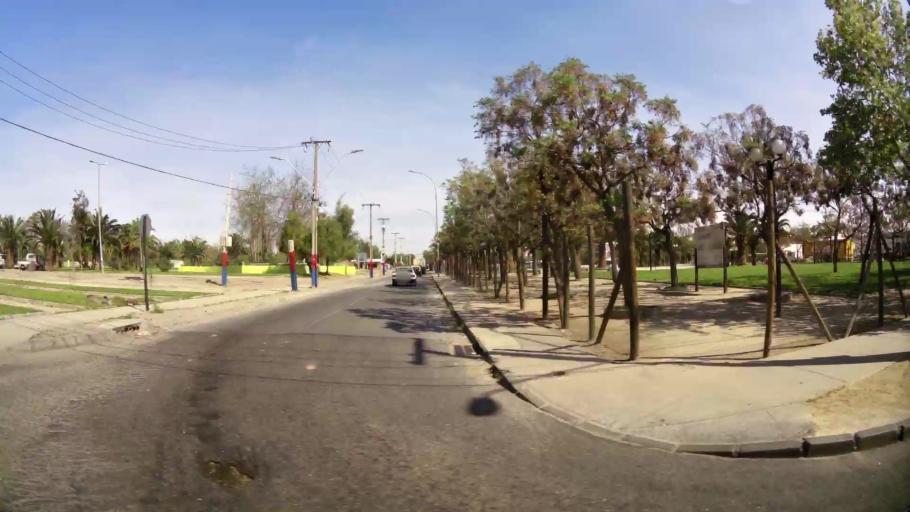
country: CL
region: Santiago Metropolitan
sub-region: Provincia de Santiago
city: La Pintana
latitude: -33.5413
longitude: -70.6444
